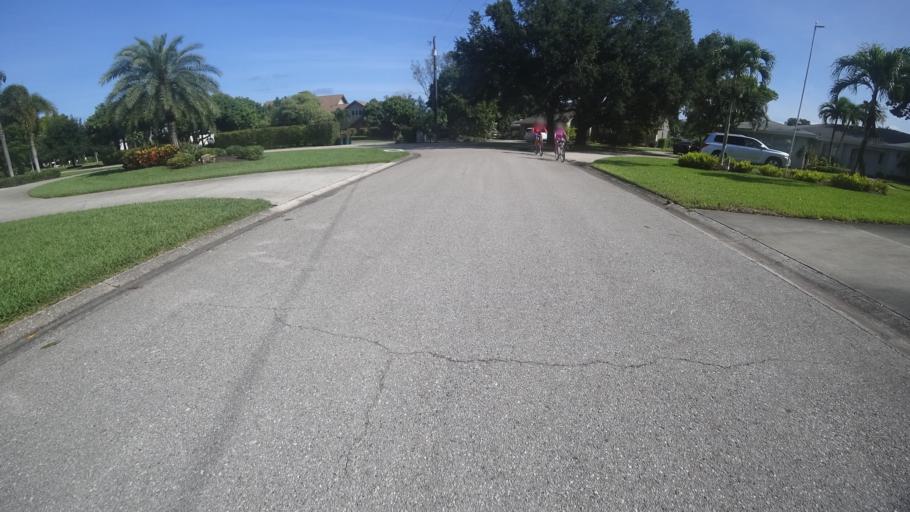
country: US
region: Florida
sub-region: Manatee County
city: West Bradenton
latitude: 27.5049
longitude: -82.6272
